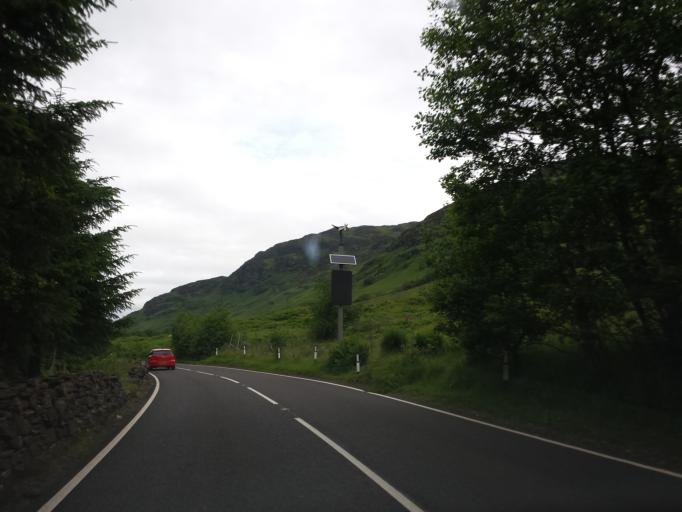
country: GB
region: Scotland
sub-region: Stirling
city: Callander
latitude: 56.3982
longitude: -4.2971
